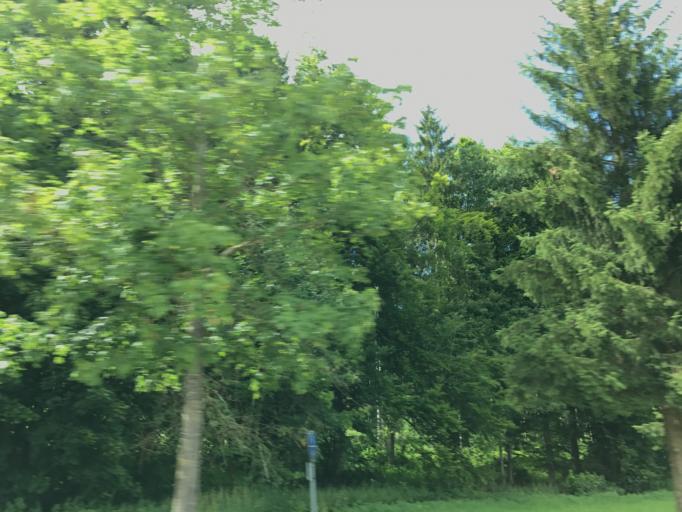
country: DE
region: Baden-Wuerttemberg
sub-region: Tuebingen Region
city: Boms
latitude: 47.9766
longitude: 9.5098
